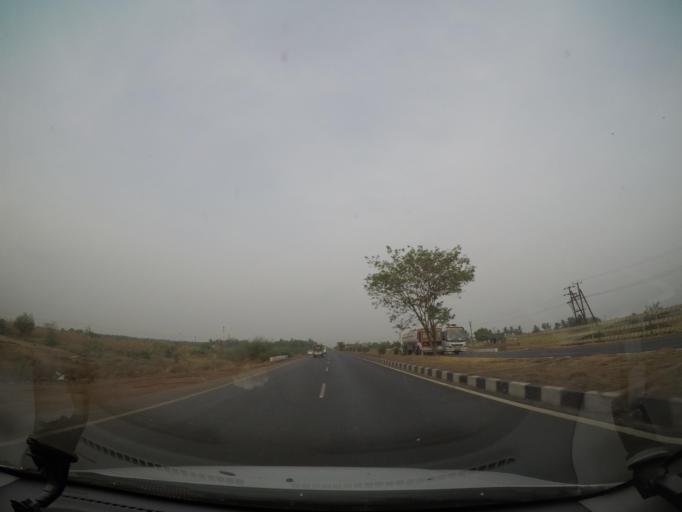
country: IN
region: Andhra Pradesh
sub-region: Krishna
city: Gannavaram
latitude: 16.6272
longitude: 80.9416
